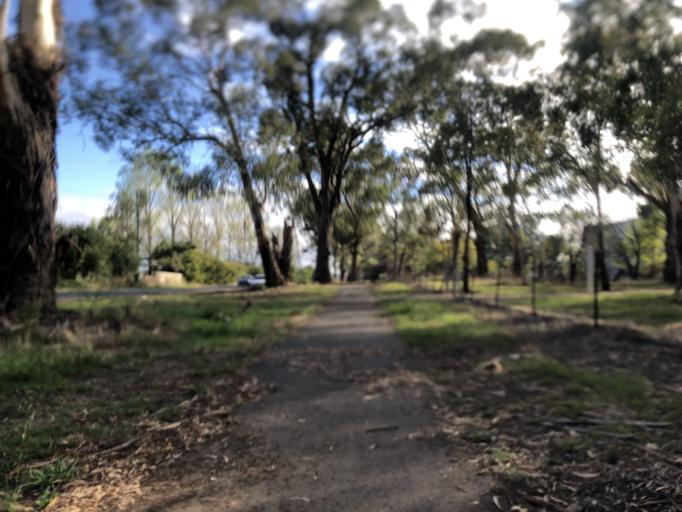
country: AU
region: New South Wales
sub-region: Orange Municipality
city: Orange
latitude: -33.3206
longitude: 149.0877
